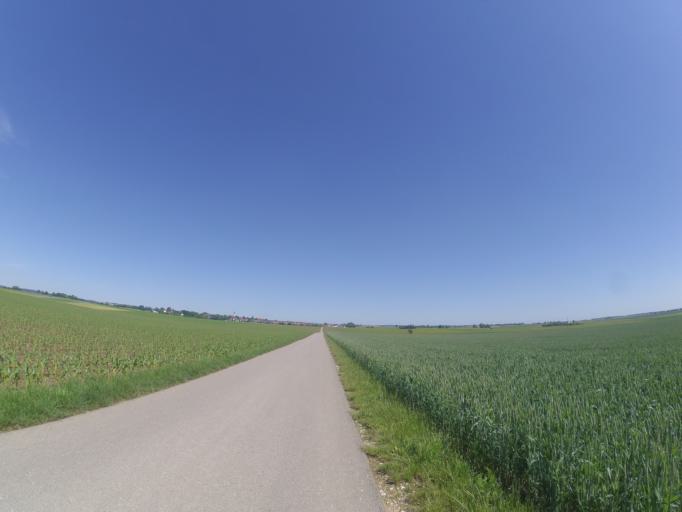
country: DE
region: Baden-Wuerttemberg
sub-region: Tuebingen Region
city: Dornstadt
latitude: 48.4700
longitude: 9.9165
